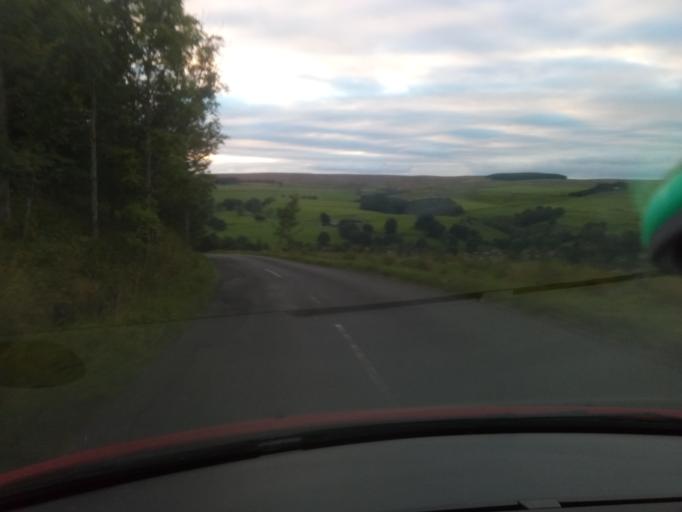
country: GB
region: England
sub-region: Northumberland
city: Bardon Mill
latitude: 54.9083
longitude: -2.3375
